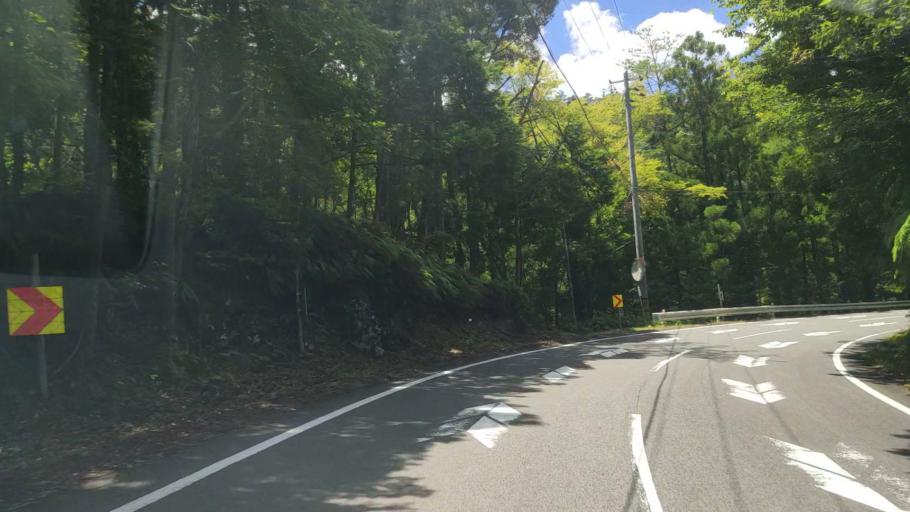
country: JP
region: Mie
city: Owase
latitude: 33.9955
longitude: 136.0133
